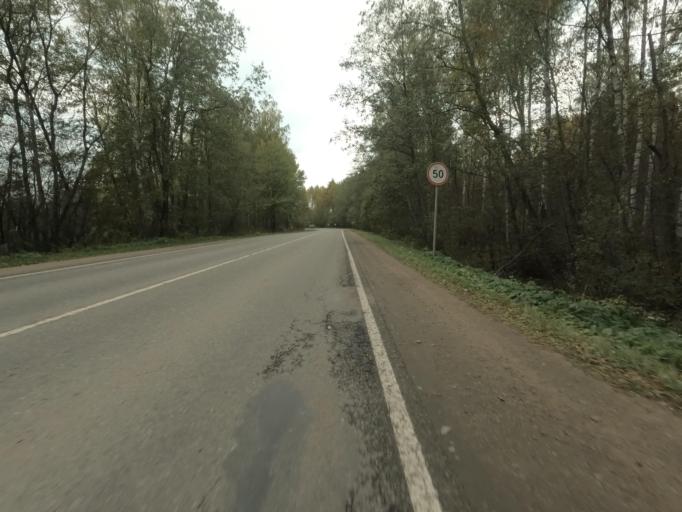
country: RU
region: Leningrad
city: Pavlovo
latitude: 59.8002
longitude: 30.9424
